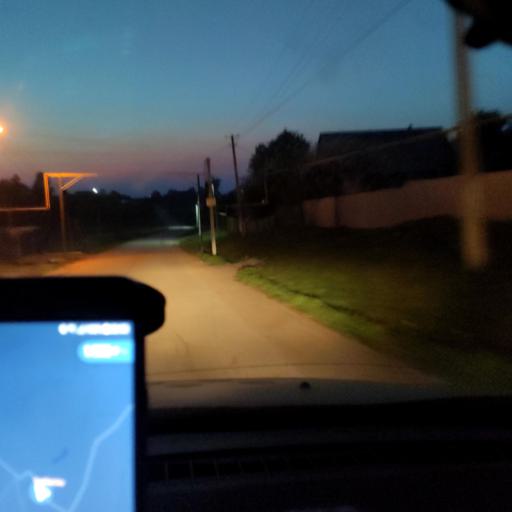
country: RU
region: Bashkortostan
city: Kabakovo
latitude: 54.6537
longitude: 56.3035
